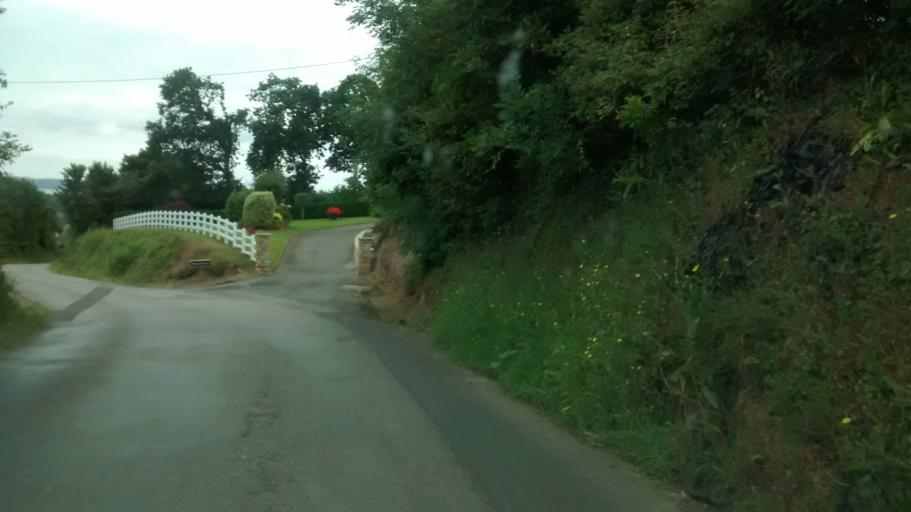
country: FR
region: Brittany
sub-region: Departement du Finistere
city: Plougastel-Daoulas
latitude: 48.3544
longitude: -4.3896
